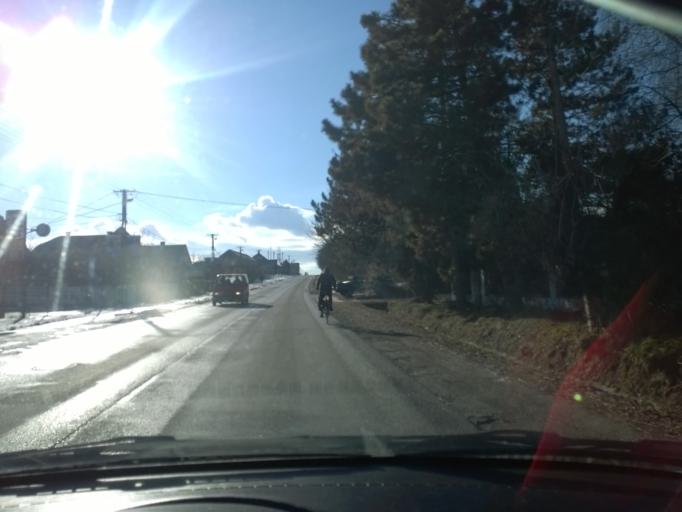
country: HU
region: Fejer
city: Baracska
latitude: 47.2834
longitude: 18.7536
